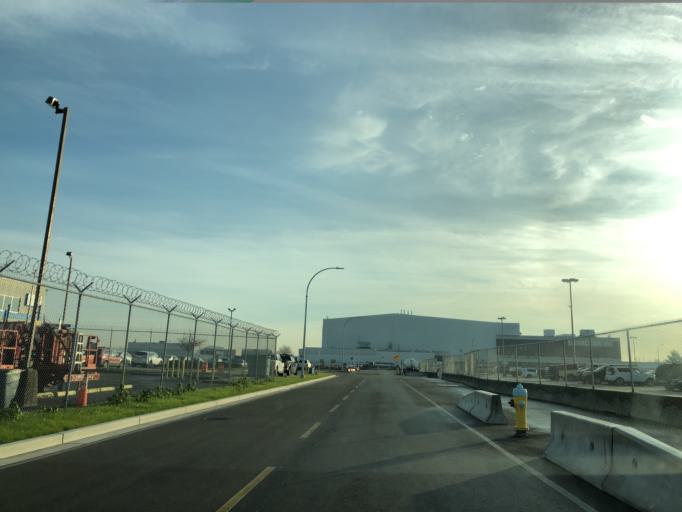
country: CA
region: British Columbia
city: Richmond
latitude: 49.1967
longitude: -123.1642
